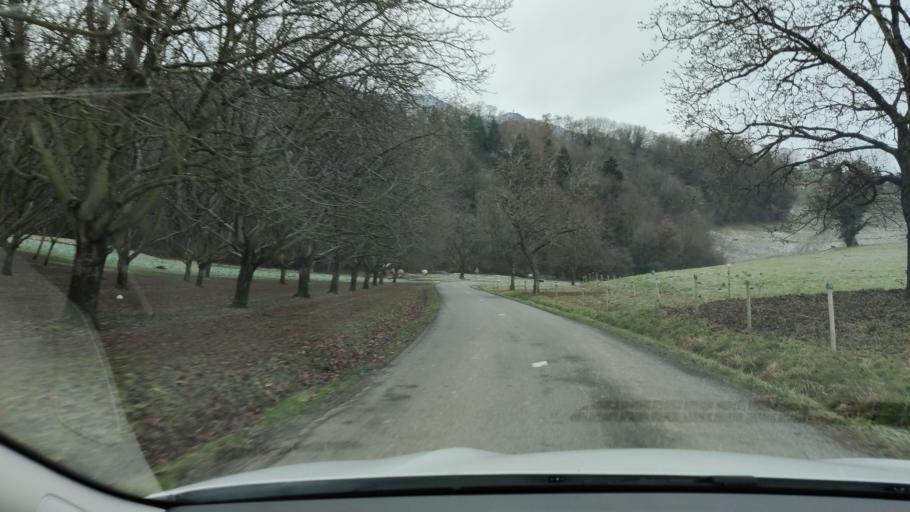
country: FR
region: Rhone-Alpes
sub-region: Departement de la Savoie
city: Montmelian
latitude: 45.4557
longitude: 6.0630
